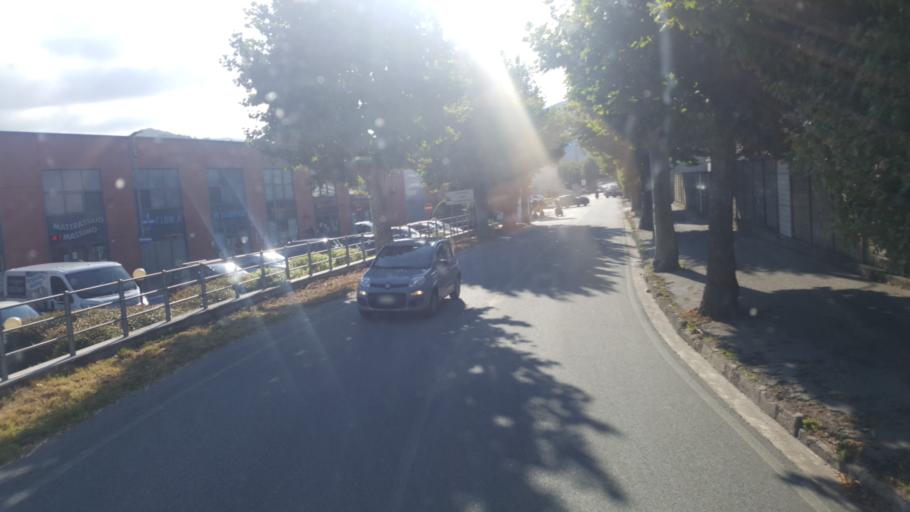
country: IT
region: Liguria
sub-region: Provincia di Genova
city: Busalla
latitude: 44.5705
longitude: 8.9550
